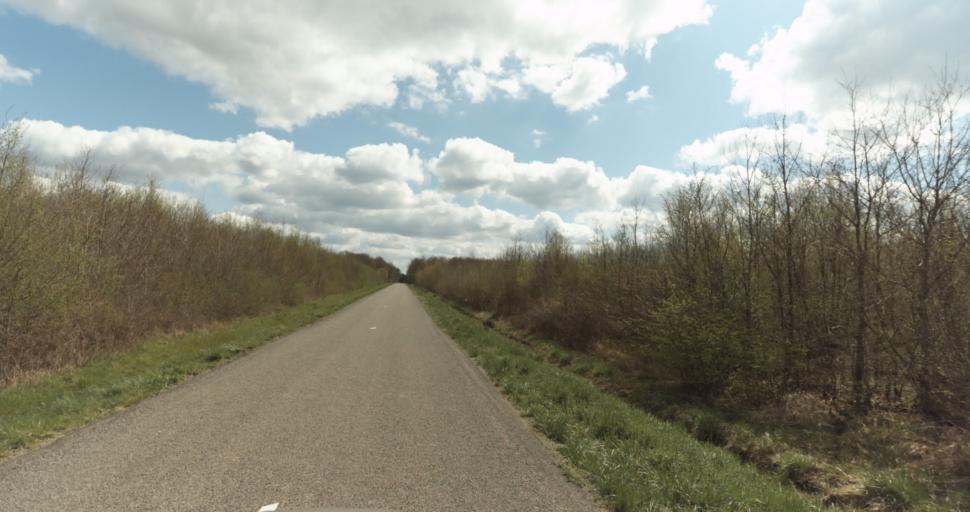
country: FR
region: Bourgogne
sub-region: Departement de la Cote-d'Or
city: Auxonne
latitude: 47.1708
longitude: 5.4331
